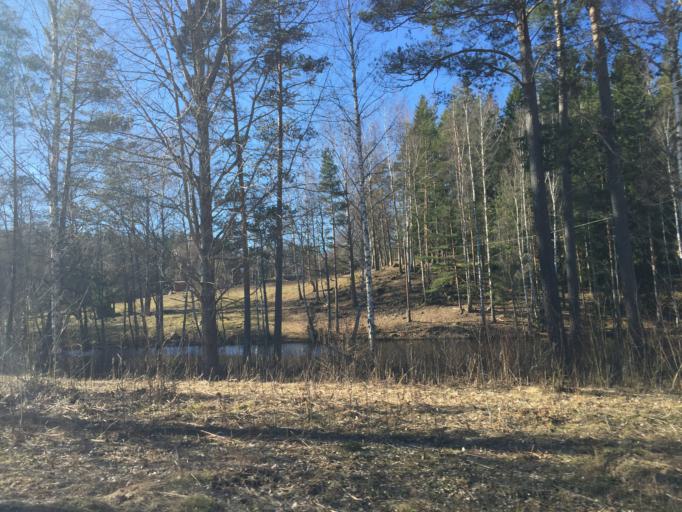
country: SE
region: OEstergoetland
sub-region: Finspangs Kommun
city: Finspang
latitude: 58.7473
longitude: 15.8282
